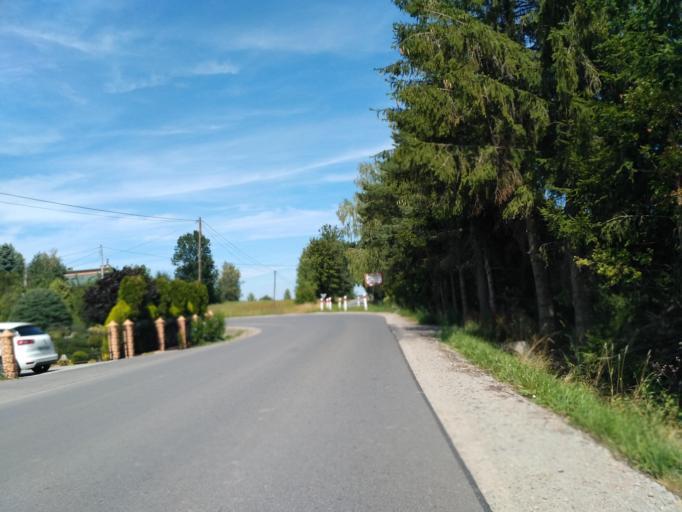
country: PL
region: Subcarpathian Voivodeship
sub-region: Powiat sanocki
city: Strachocina
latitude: 49.5785
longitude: 22.1225
